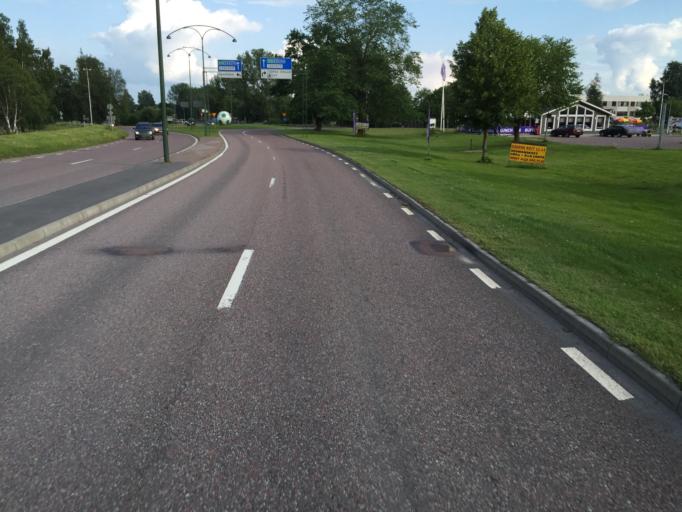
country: SE
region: Dalarna
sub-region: Borlange Kommun
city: Borlaenge
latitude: 60.4961
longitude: 15.4006
